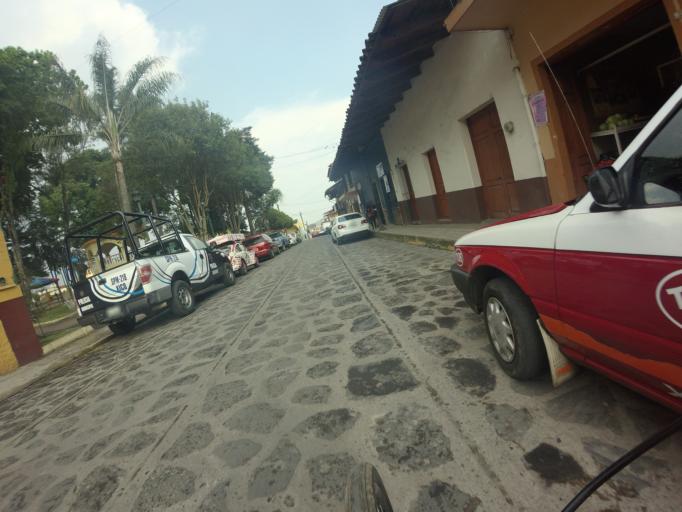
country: MX
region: Veracruz
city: Xico
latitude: 19.4223
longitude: -97.0116
